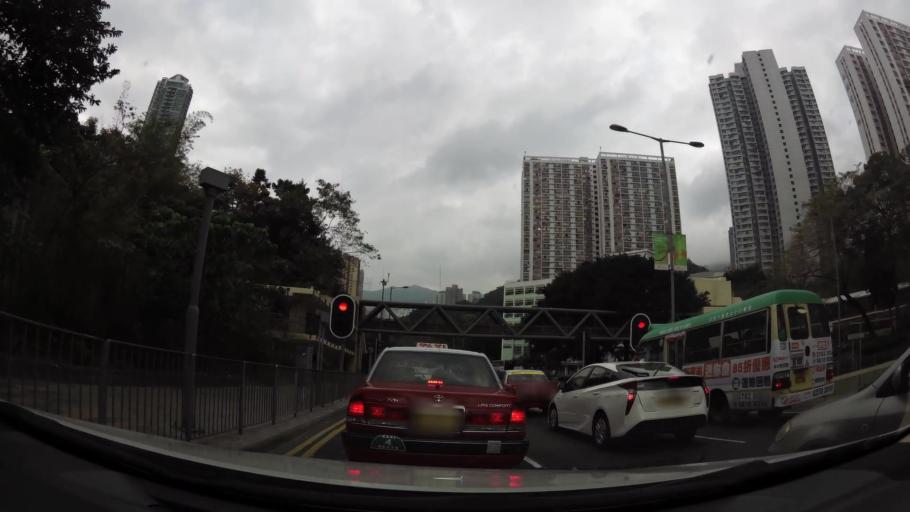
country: HK
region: Kowloon City
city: Kowloon
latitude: 22.3332
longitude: 114.2126
